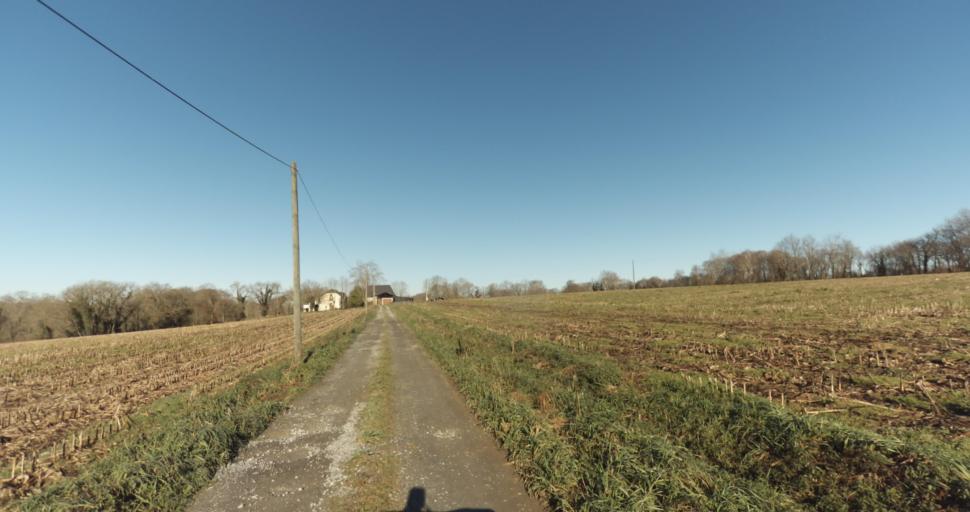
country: FR
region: Aquitaine
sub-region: Departement des Pyrenees-Atlantiques
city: Morlaas
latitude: 43.3449
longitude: -0.2461
